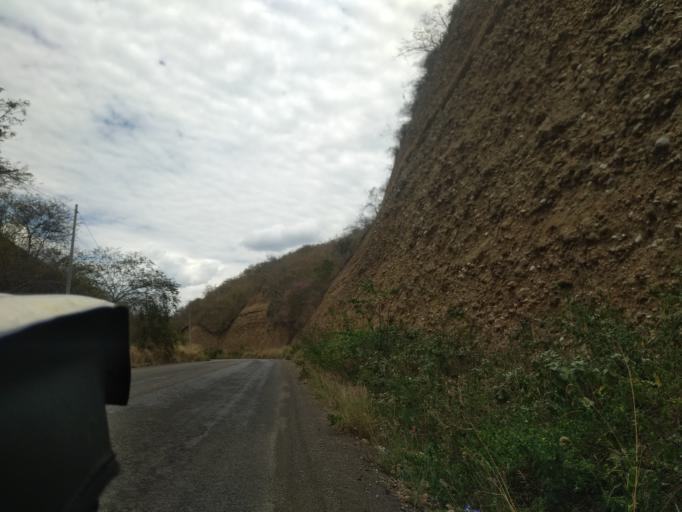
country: PE
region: Cajamarca
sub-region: Provincia de San Ignacio
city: La Coipa
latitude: -5.3910
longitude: -78.7786
